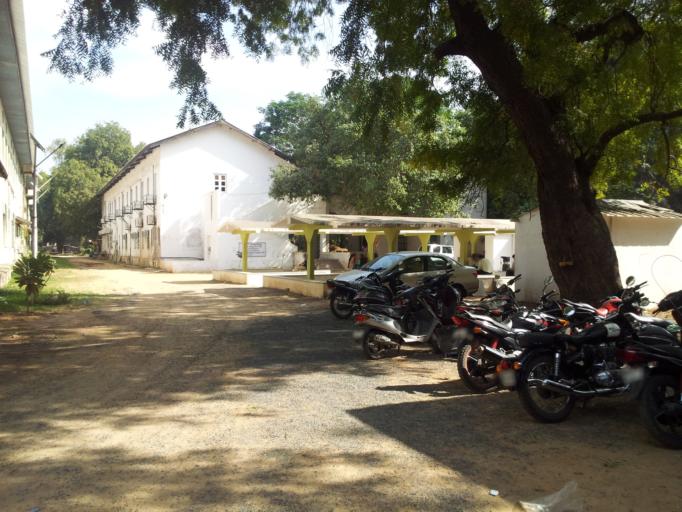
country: IN
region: Gujarat
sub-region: Ahmadabad
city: Ahmedabad
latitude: 23.0349
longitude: 72.5512
